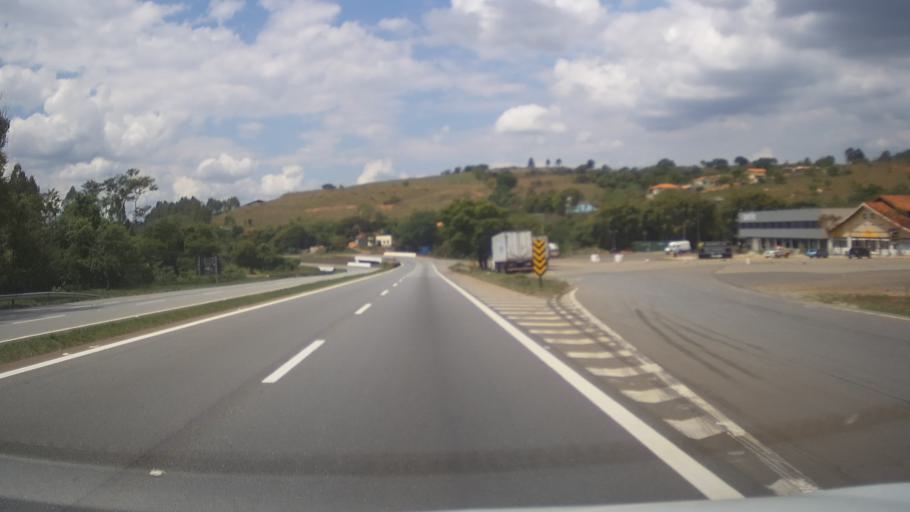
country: BR
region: Minas Gerais
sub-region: Nepomuceno
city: Nepomuceno
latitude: -21.3008
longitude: -45.1526
